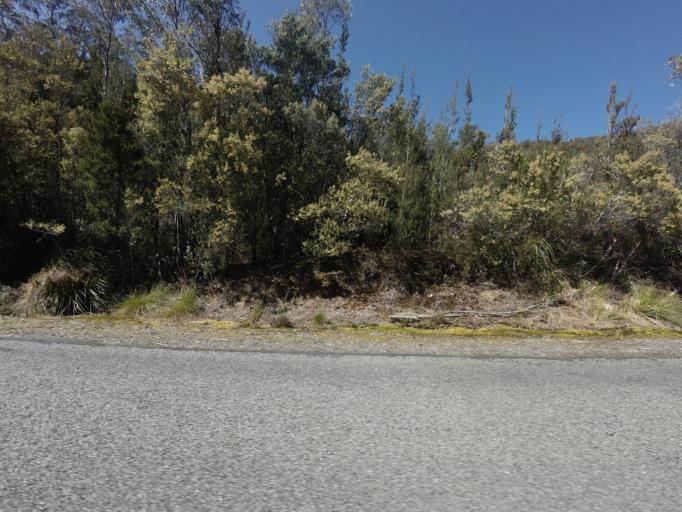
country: AU
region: Tasmania
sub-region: Huon Valley
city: Geeveston
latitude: -42.8021
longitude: 146.3943
